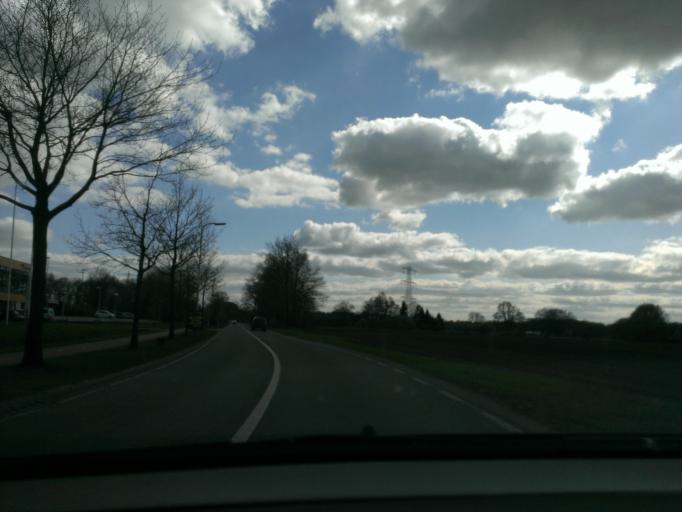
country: NL
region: Overijssel
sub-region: Gemeente Borne
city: Borne
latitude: 52.3016
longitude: 6.7291
